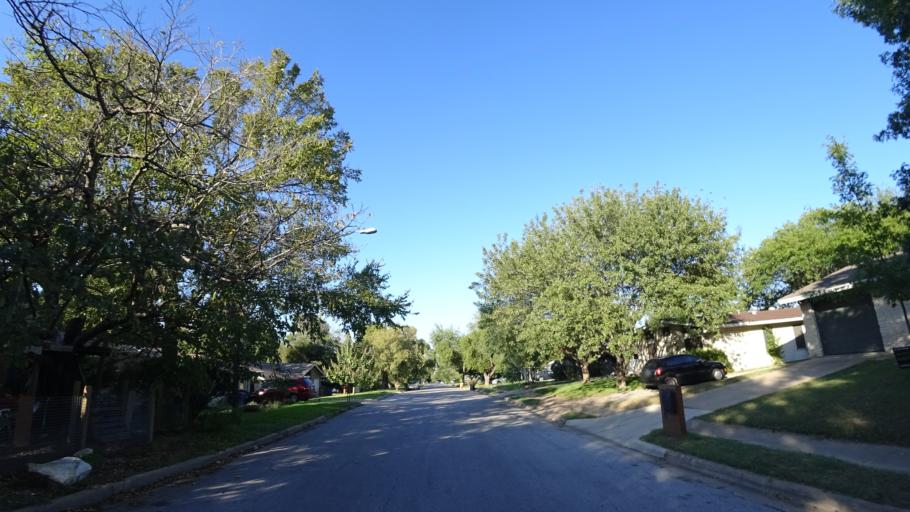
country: US
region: Texas
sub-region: Travis County
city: Austin
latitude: 30.2193
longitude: -97.7385
